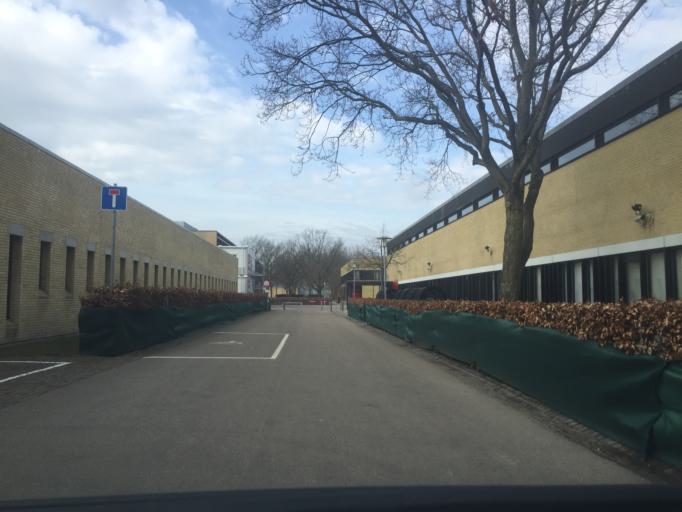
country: DK
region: Capital Region
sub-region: Lyngby-Tarbaek Kommune
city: Kongens Lyngby
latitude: 55.7845
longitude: 12.5201
